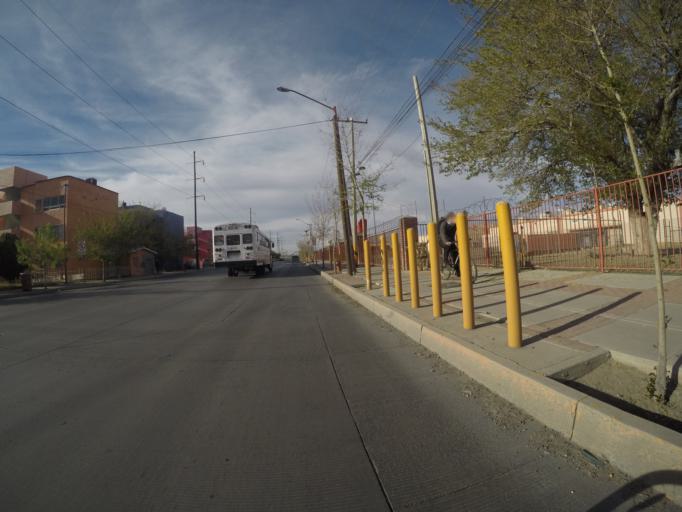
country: MX
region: Chihuahua
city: Ciudad Juarez
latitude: 31.7515
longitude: -106.4412
